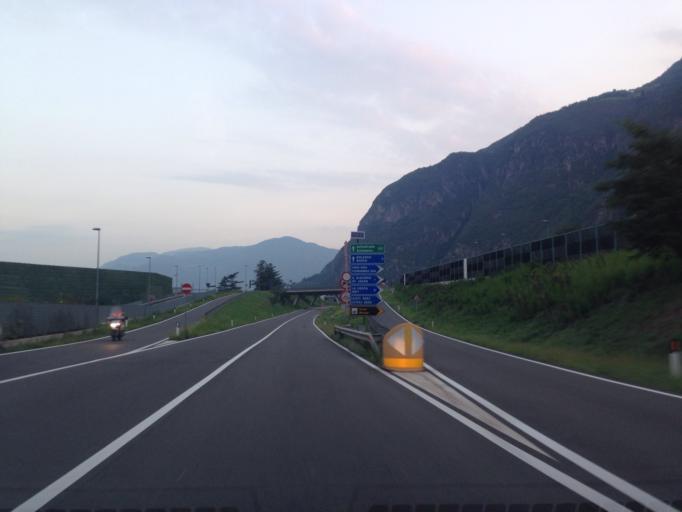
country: IT
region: Trentino-Alto Adige
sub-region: Bolzano
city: Pineta
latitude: 46.4404
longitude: 11.3438
